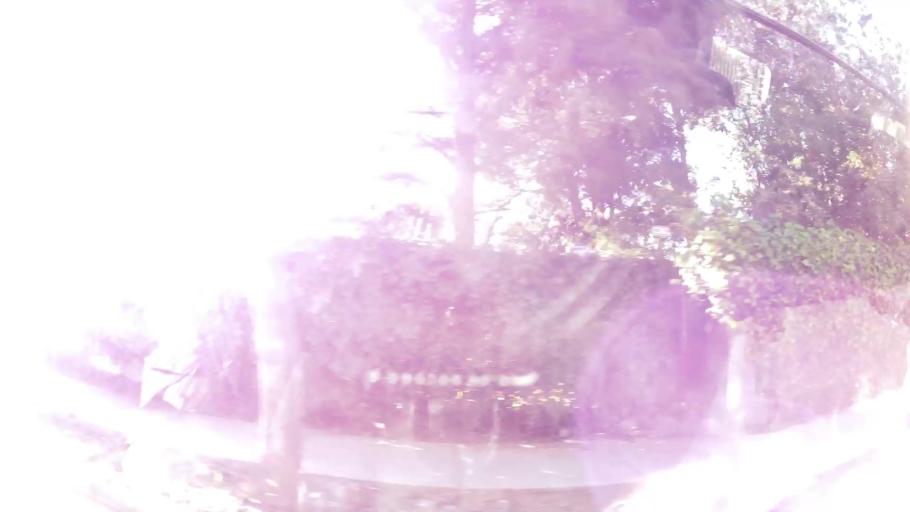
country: CL
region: Santiago Metropolitan
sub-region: Provincia de Santiago
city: Villa Presidente Frei, Nunoa, Santiago, Chile
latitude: -33.3614
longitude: -70.5125
